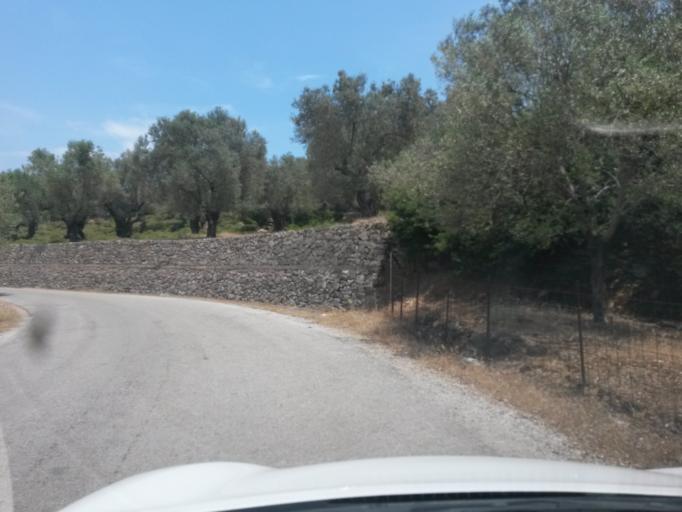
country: GR
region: North Aegean
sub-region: Nomos Lesvou
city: Pamfylla
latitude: 39.1720
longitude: 26.4843
